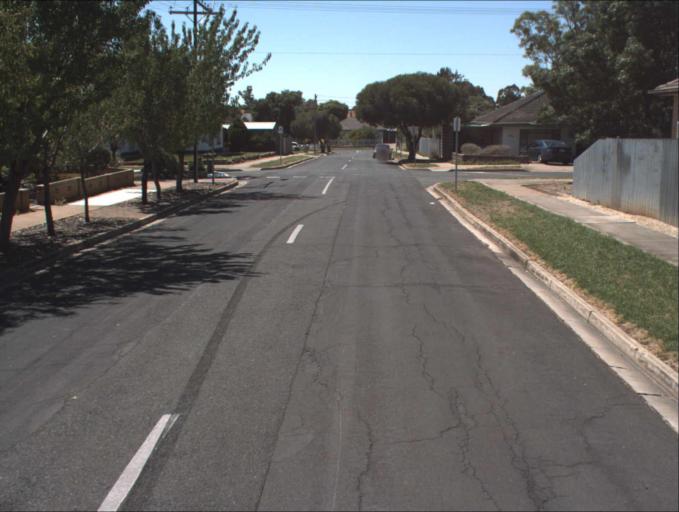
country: AU
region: South Australia
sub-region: Port Adelaide Enfield
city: Enfield
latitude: -34.8667
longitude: 138.6147
